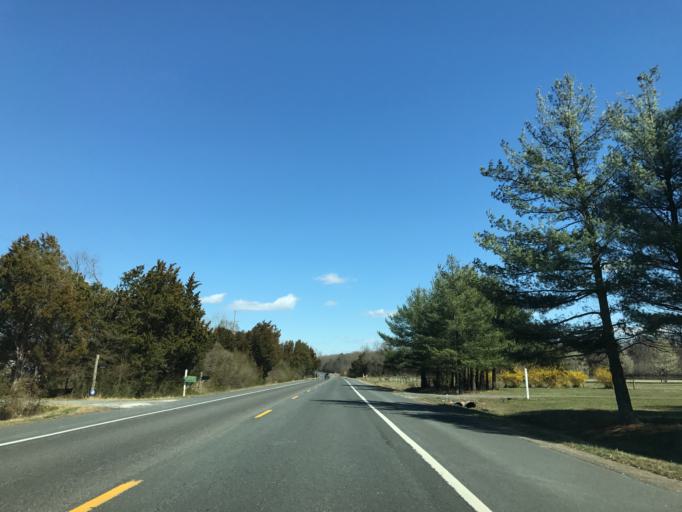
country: US
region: Maryland
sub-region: Queen Anne's County
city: Kingstown
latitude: 39.2244
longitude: -75.9357
